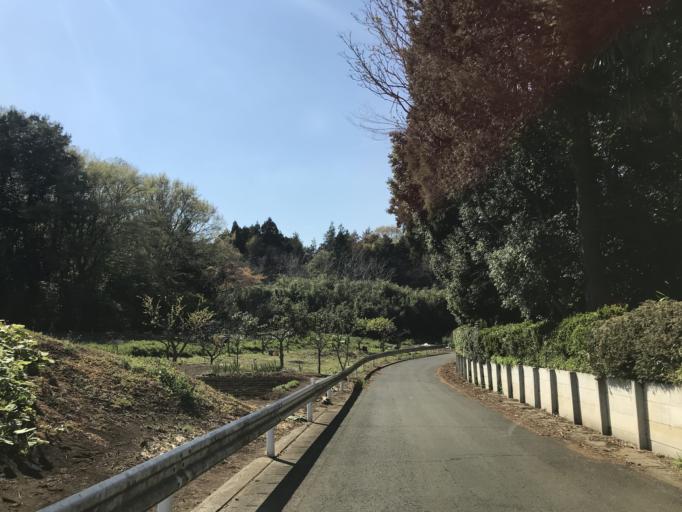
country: JP
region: Ibaraki
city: Moriya
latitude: 35.9545
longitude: 139.9723
